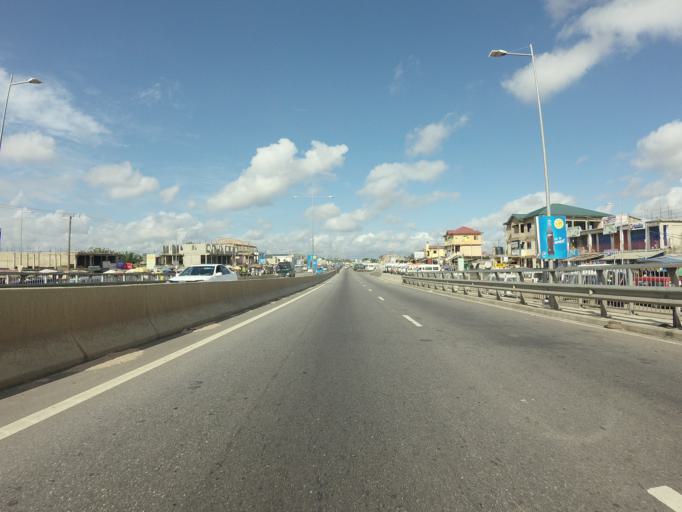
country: GH
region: Central
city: Kasoa
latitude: 5.5339
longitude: -0.4272
